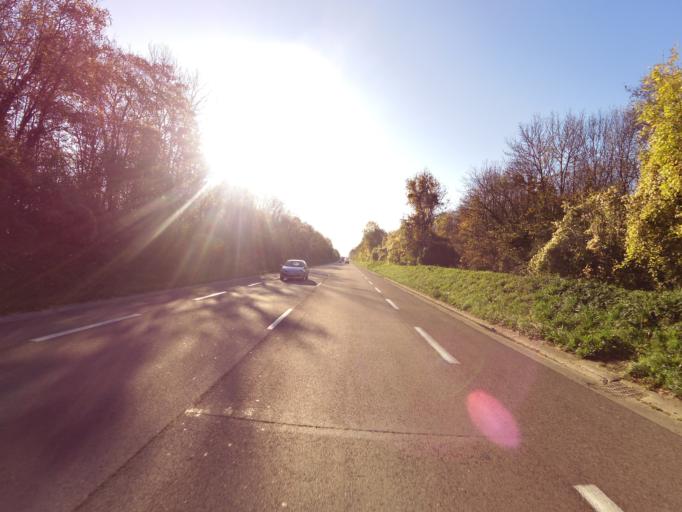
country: FR
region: Champagne-Ardenne
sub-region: Departement de l'Aube
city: Bucheres
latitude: 48.2414
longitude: 4.1193
